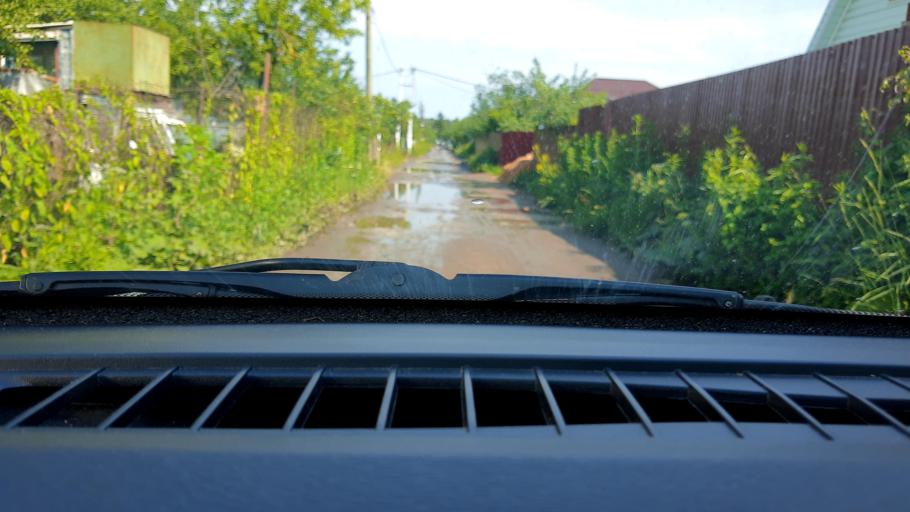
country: RU
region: Nizjnij Novgorod
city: Gorbatovka
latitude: 56.3169
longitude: 43.8295
